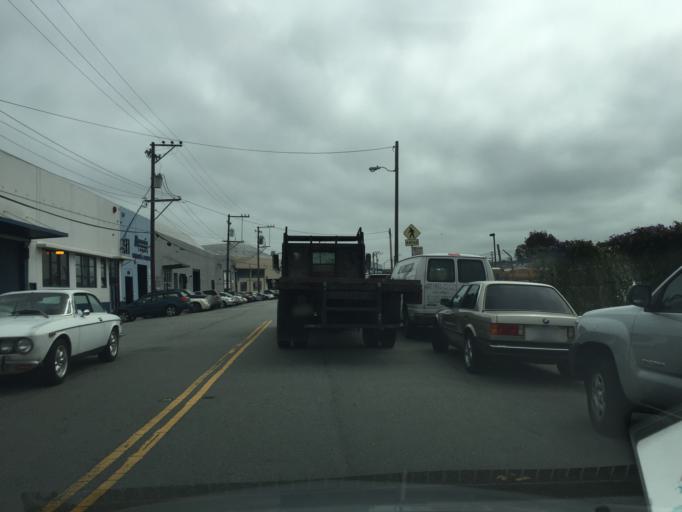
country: US
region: California
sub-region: San Francisco County
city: San Francisco
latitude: 37.7467
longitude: -122.3998
